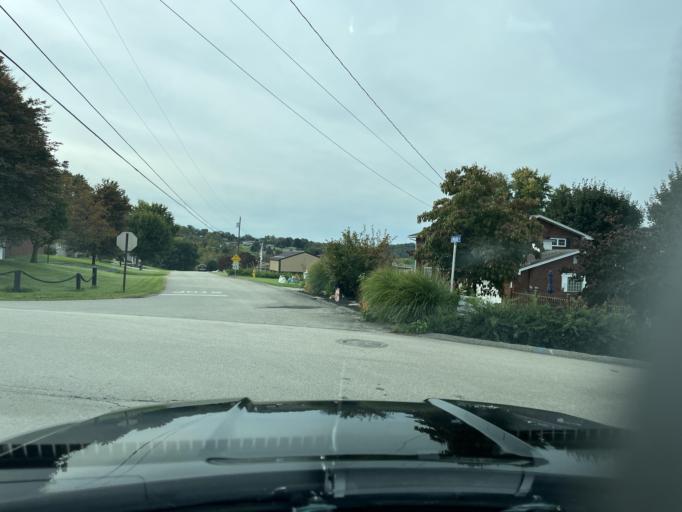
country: US
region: Pennsylvania
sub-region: Fayette County
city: South Uniontown
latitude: 39.8847
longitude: -79.7417
